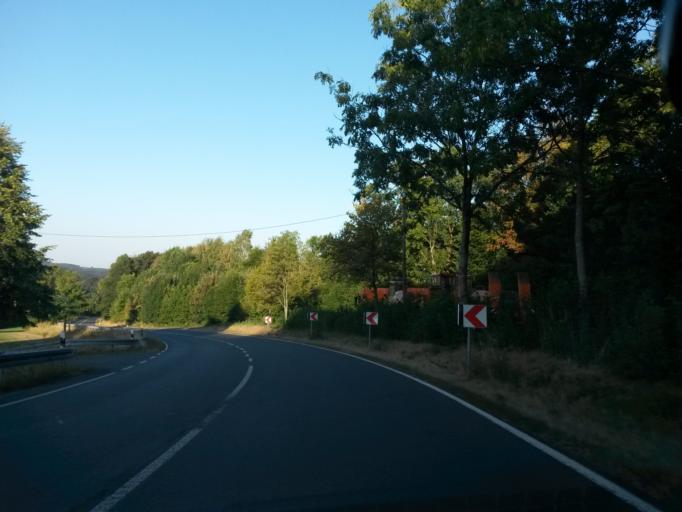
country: DE
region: North Rhine-Westphalia
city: Kierspe
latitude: 51.1198
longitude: 7.5591
